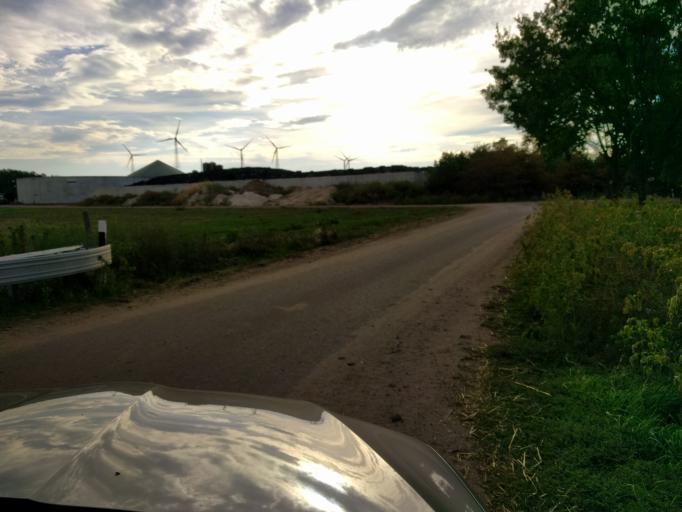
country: DE
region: Brandenburg
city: Ziesar
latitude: 52.2130
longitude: 12.2932
